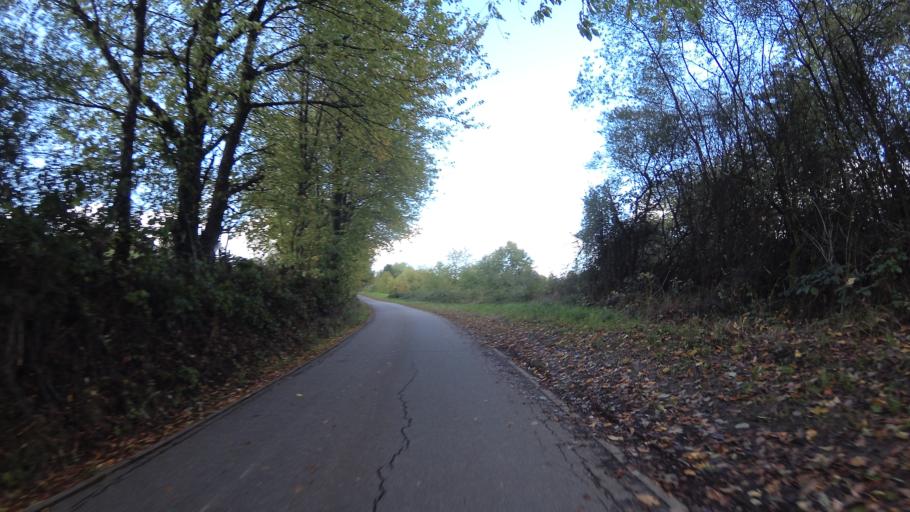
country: DE
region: Saarland
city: Tholey
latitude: 49.4749
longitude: 7.0406
